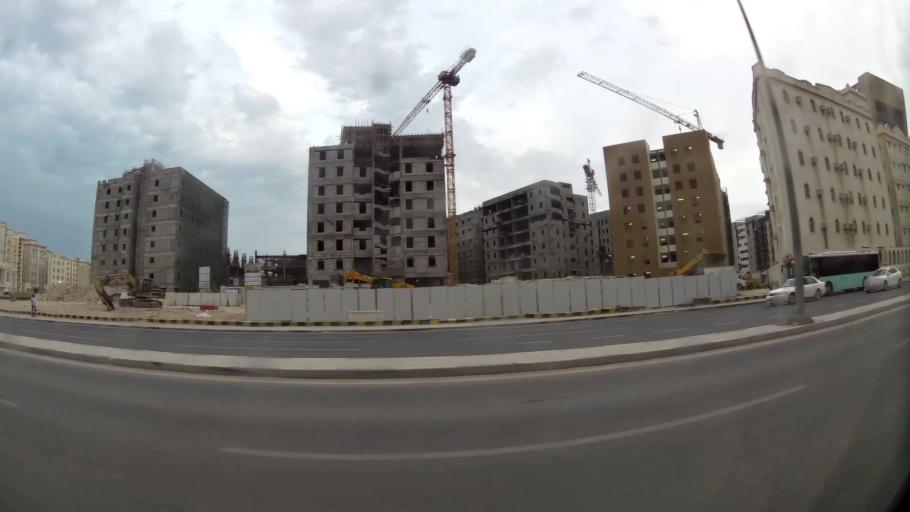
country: QA
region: Baladiyat ad Dawhah
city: Doha
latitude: 25.2677
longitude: 51.5259
